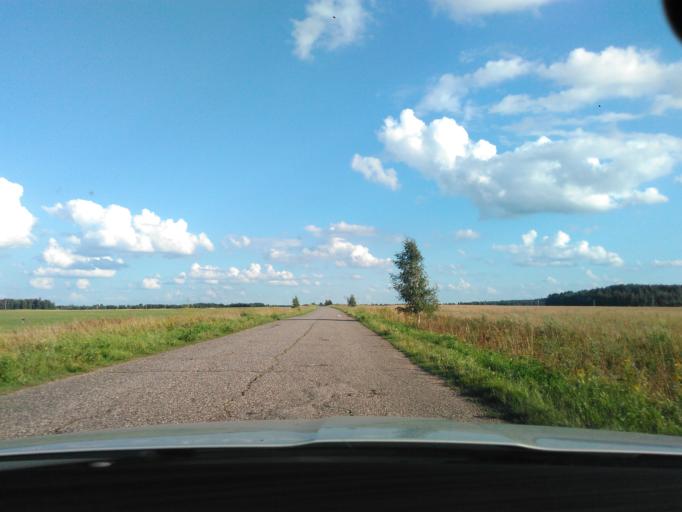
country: RU
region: Tverskaya
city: Zavidovo
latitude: 56.6067
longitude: 36.5924
